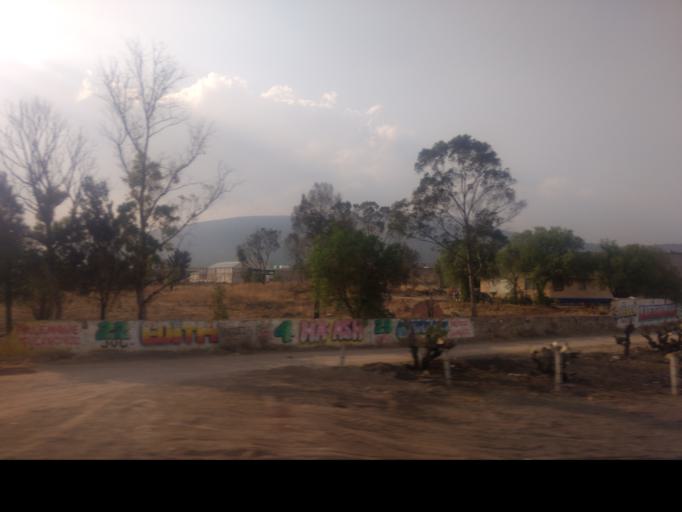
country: MX
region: Mexico
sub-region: San Martin de las Piramides
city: San Pablo Ixquitlan
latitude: 19.7178
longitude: -98.7917
